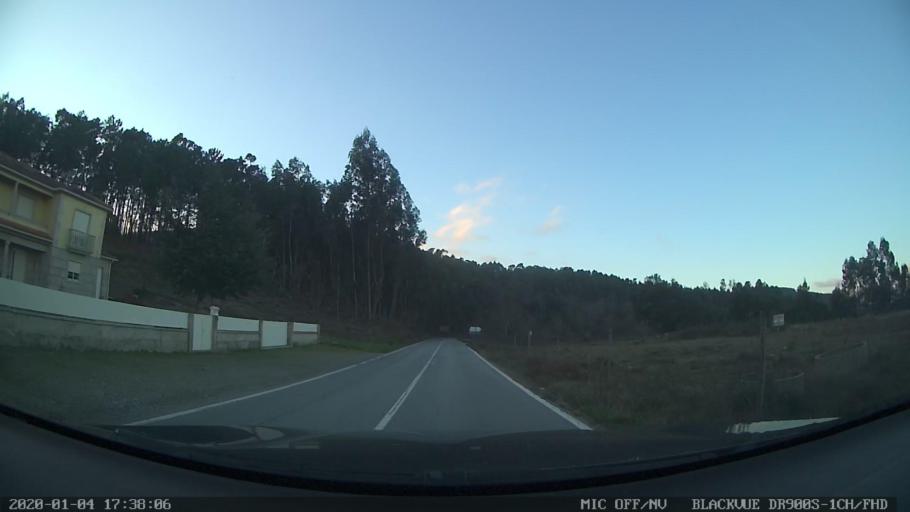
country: PT
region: Vila Real
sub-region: Mondim de Basto
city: Mondim de Basto
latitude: 41.4530
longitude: -7.9591
